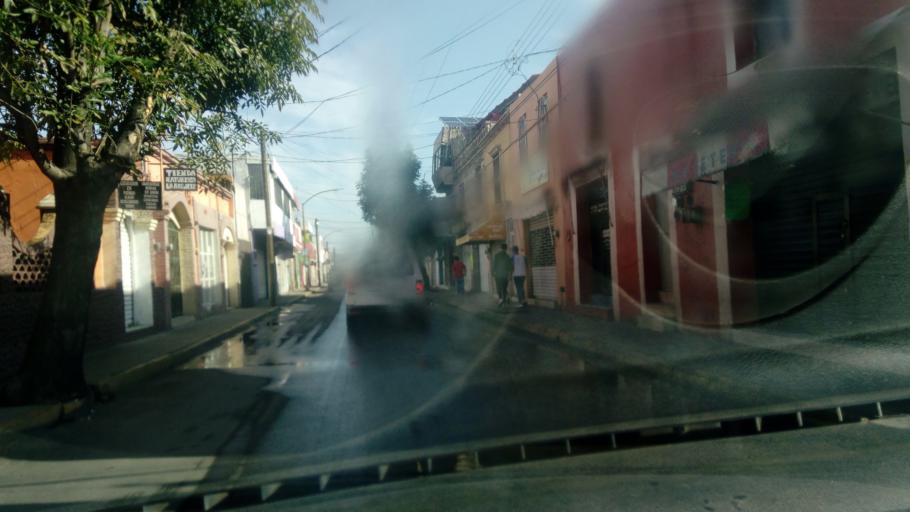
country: MX
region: Durango
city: Victoria de Durango
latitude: 24.0231
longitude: -104.6640
